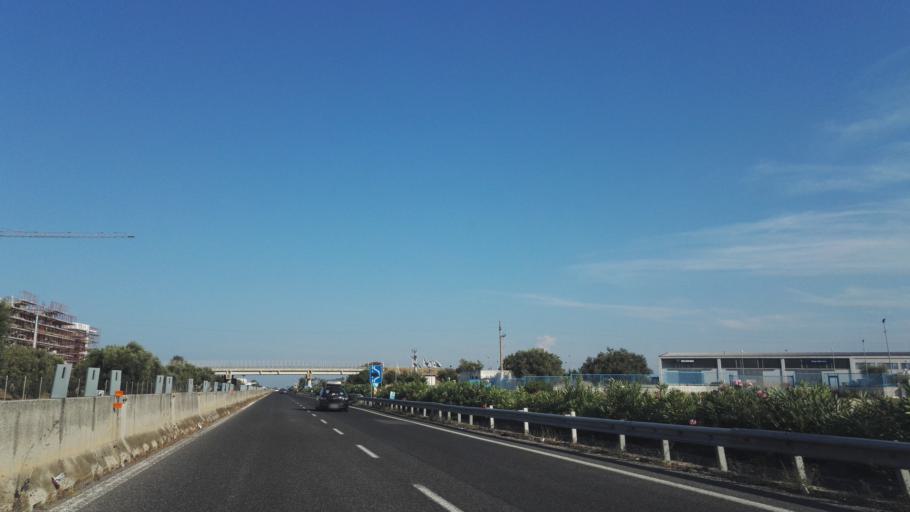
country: IT
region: Apulia
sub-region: Provincia di Bari
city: Monopoli
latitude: 40.9327
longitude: 17.2980
